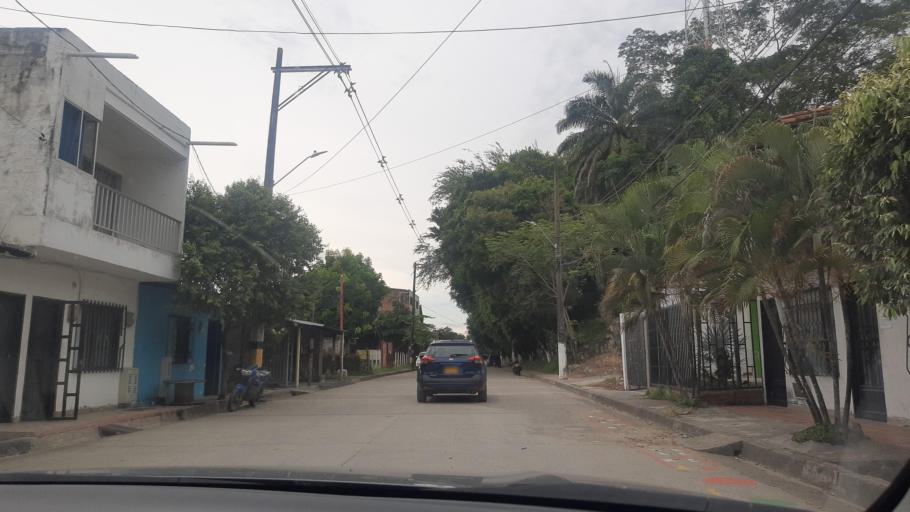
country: CO
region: Antioquia
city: Puerto Triunfo
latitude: 5.8727
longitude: -74.6408
